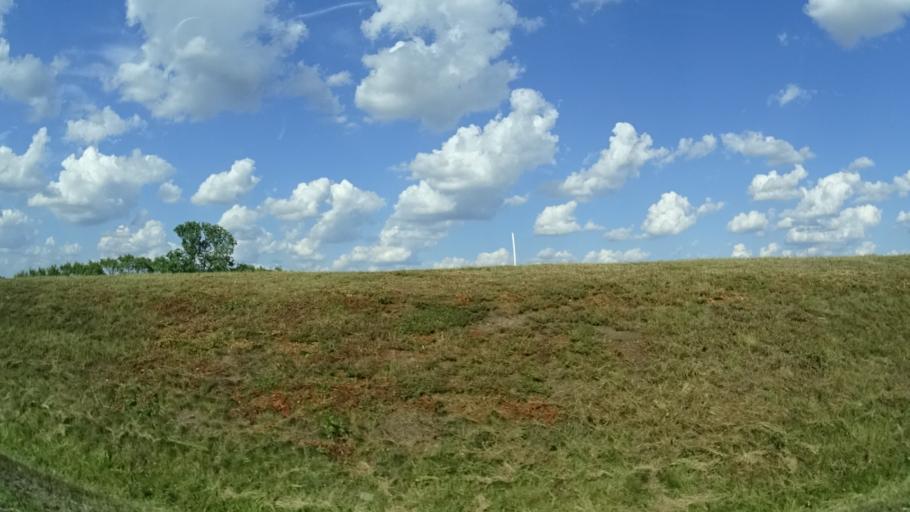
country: DE
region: Bavaria
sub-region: Regierungsbezirk Unterfranken
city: Bad Konigshofen im Grabfeld
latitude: 50.2835
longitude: 10.4899
